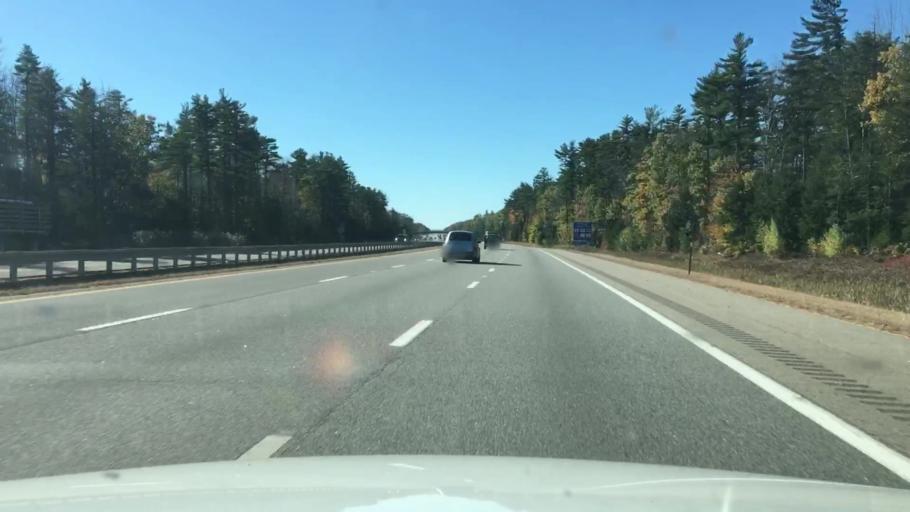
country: US
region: Maine
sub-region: York County
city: West Kennebunk
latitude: 43.4250
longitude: -70.5514
